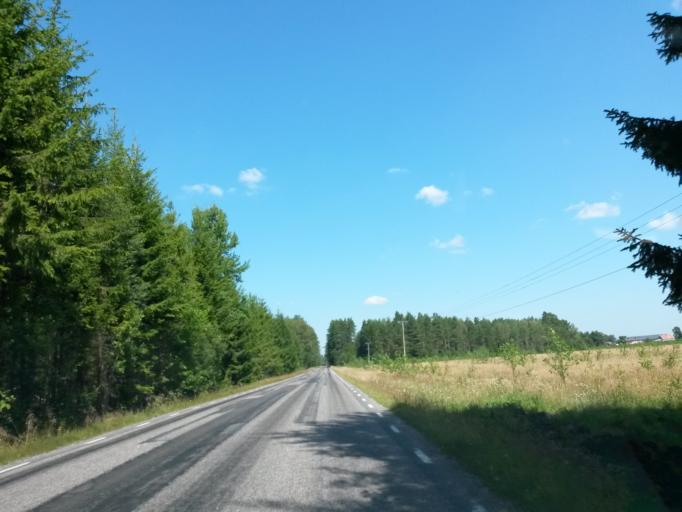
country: SE
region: Vaestra Goetaland
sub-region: Essunga Kommun
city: Nossebro
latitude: 58.1650
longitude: 12.7450
